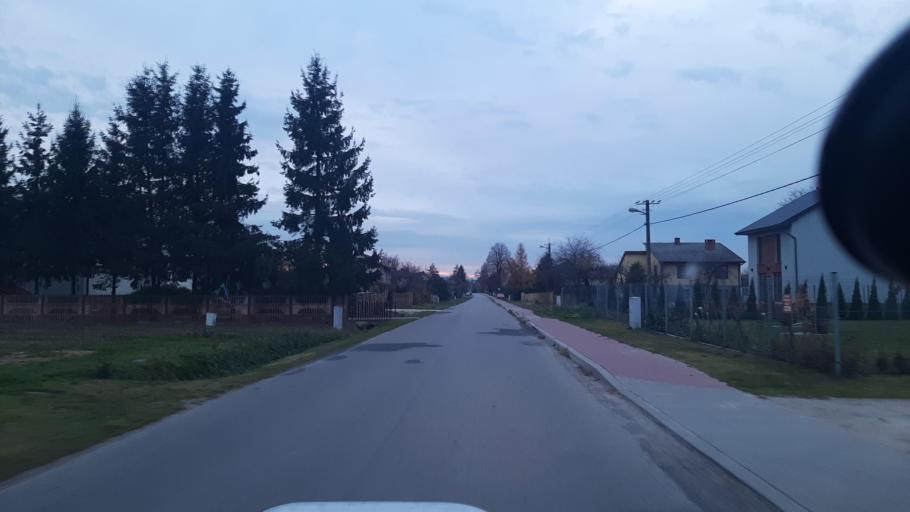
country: PL
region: Lublin Voivodeship
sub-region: Powiat lubelski
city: Garbow
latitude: 51.3614
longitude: 22.3778
